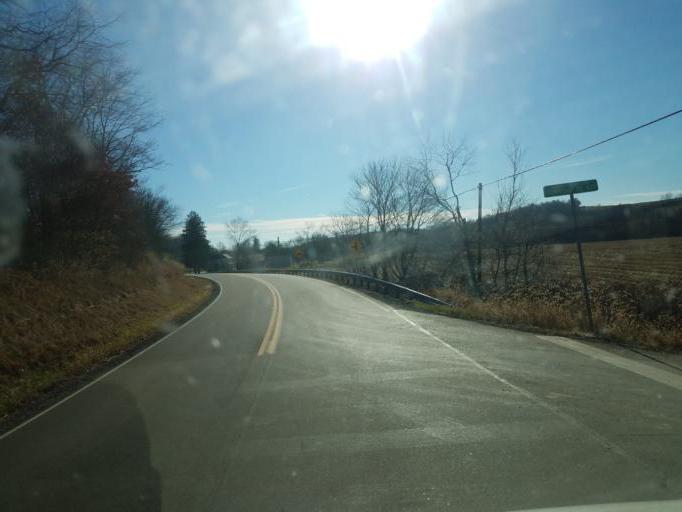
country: US
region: Ohio
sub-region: Muskingum County
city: Dresden
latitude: 40.2017
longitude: -82.0504
